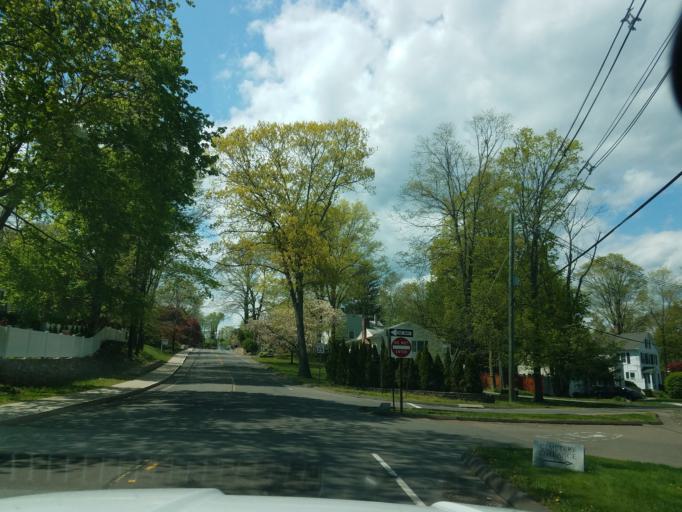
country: US
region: Connecticut
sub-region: Fairfield County
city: New Canaan
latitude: 41.1416
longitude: -73.4846
